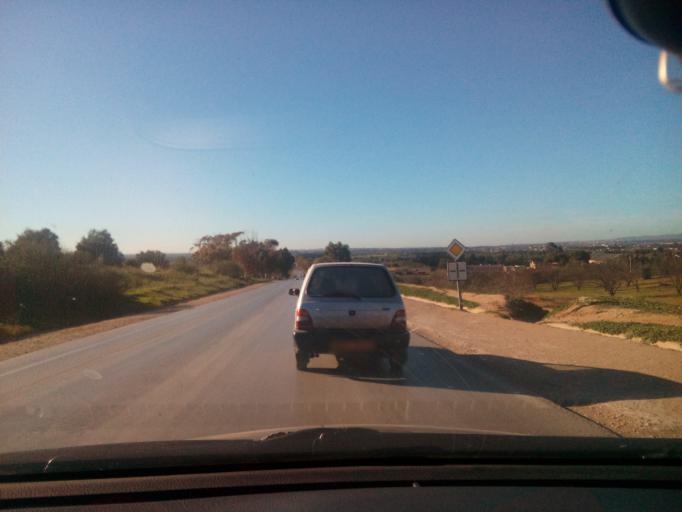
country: DZ
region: Mostaganem
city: Mostaganem
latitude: 35.8967
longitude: 0.2556
